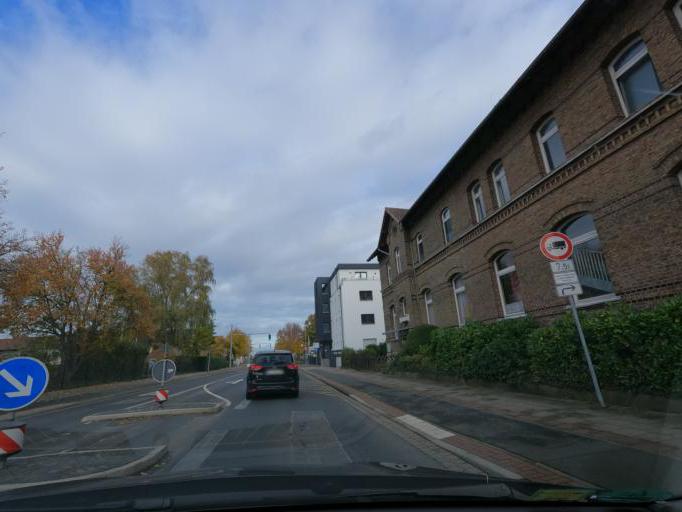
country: DE
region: Lower Saxony
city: Leiferde
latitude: 52.2229
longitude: 10.5034
